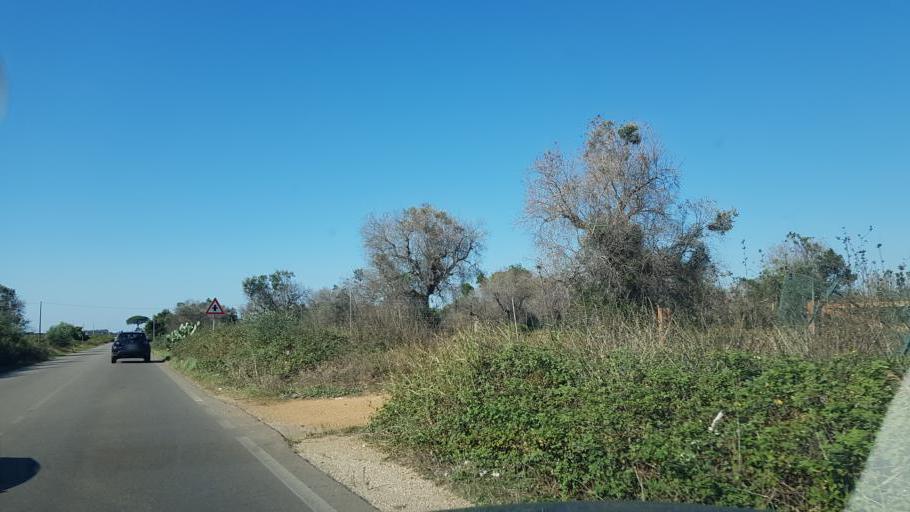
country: IT
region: Apulia
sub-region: Provincia di Lecce
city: Magliano
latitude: 40.3161
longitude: 18.0487
